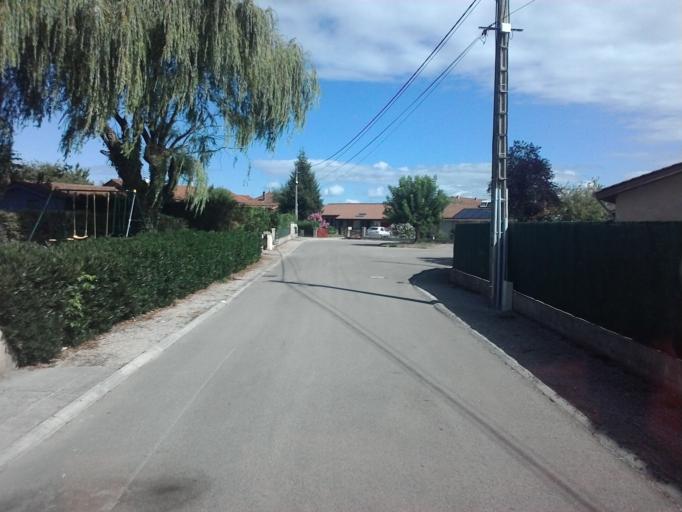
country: FR
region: Rhone-Alpes
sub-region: Departement de l'Ain
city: Ambronay
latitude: 46.0017
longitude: 5.3593
